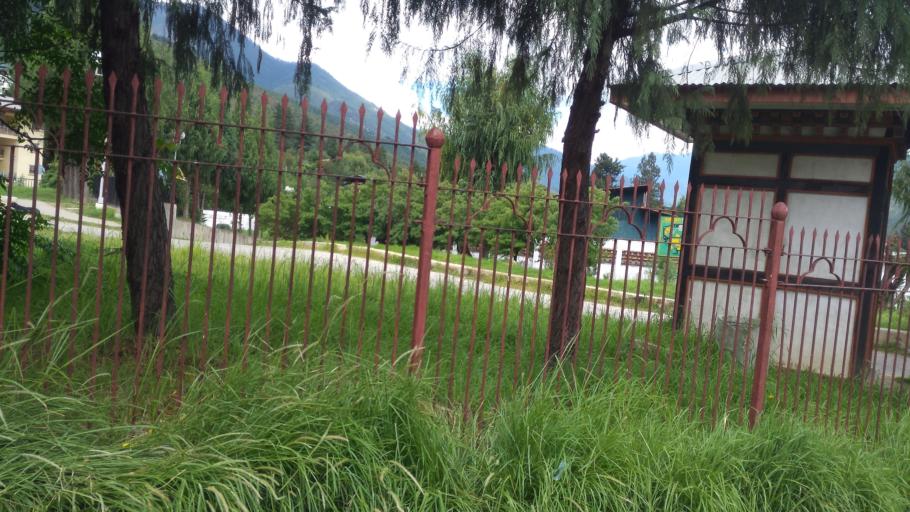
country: BT
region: Thimphu
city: Thimphu
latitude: 27.4706
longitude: 89.6328
